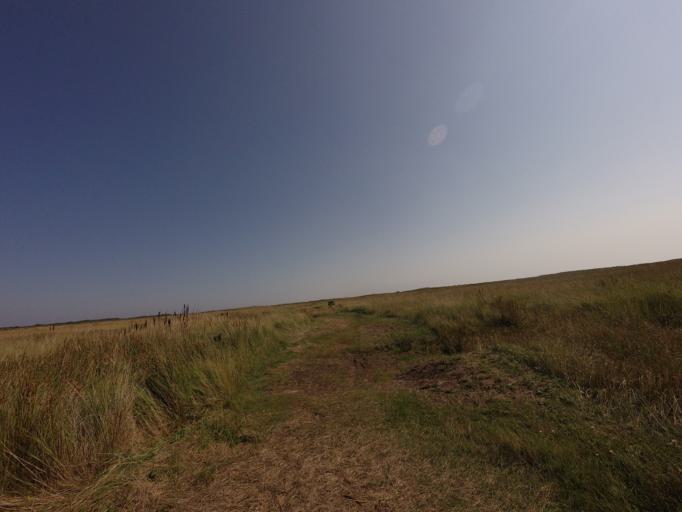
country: NL
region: Friesland
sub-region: Gemeente Schiermonnikoog
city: Schiermonnikoog
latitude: 53.4909
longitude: 6.2406
